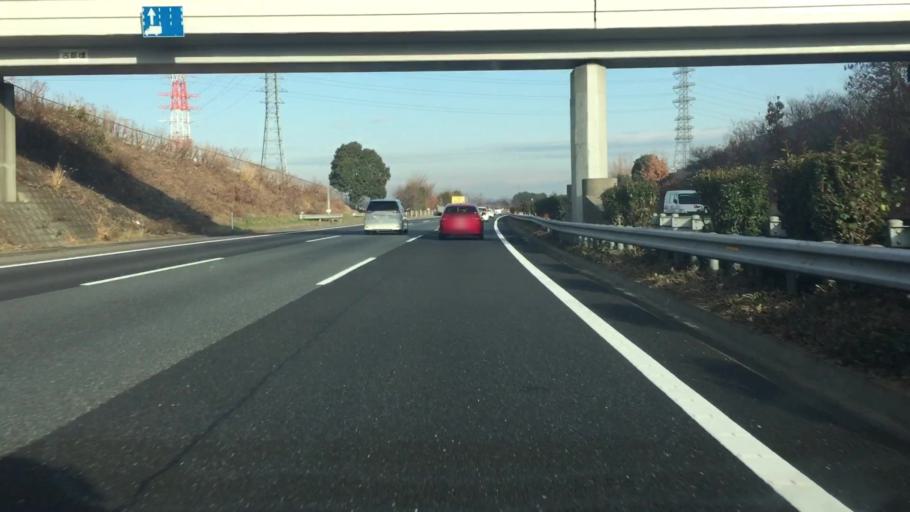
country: JP
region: Saitama
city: Kodamacho-kodamaminami
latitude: 36.1774
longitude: 139.1916
